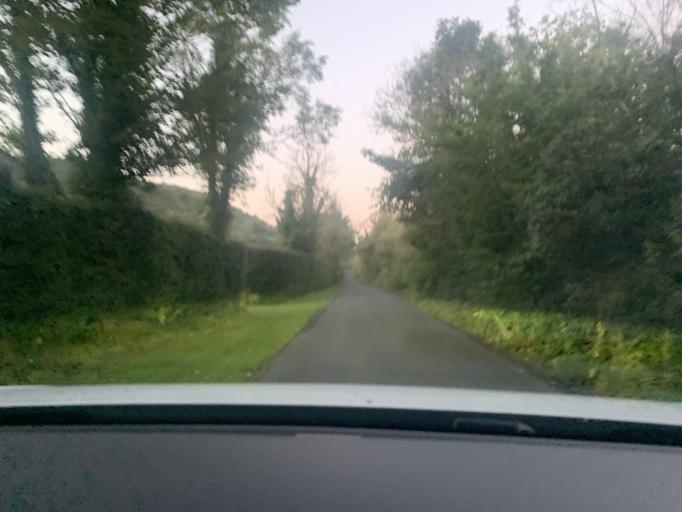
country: IE
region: Connaught
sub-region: County Leitrim
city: Manorhamilton
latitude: 54.2578
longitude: -8.3015
